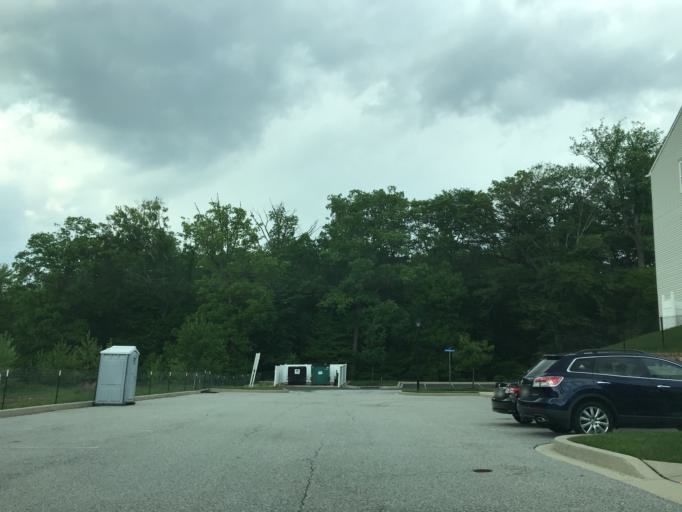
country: US
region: Maryland
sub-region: Harford County
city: North Bel Air
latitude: 39.5297
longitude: -76.3639
